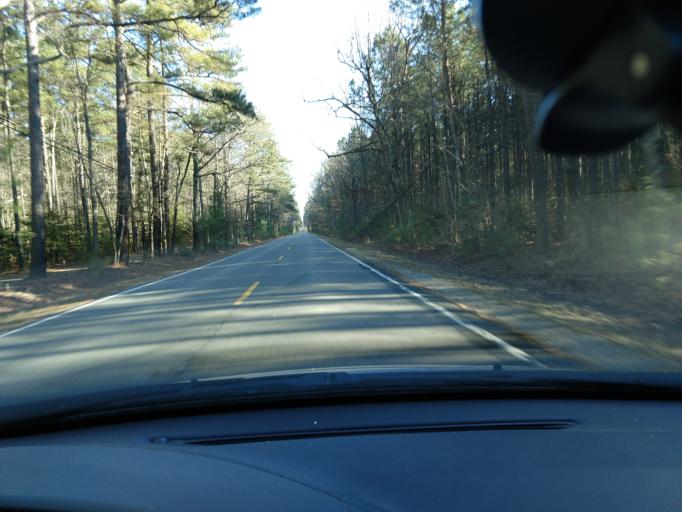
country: US
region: Virginia
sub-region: Surry County
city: Surry
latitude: 37.2720
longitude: -76.9039
